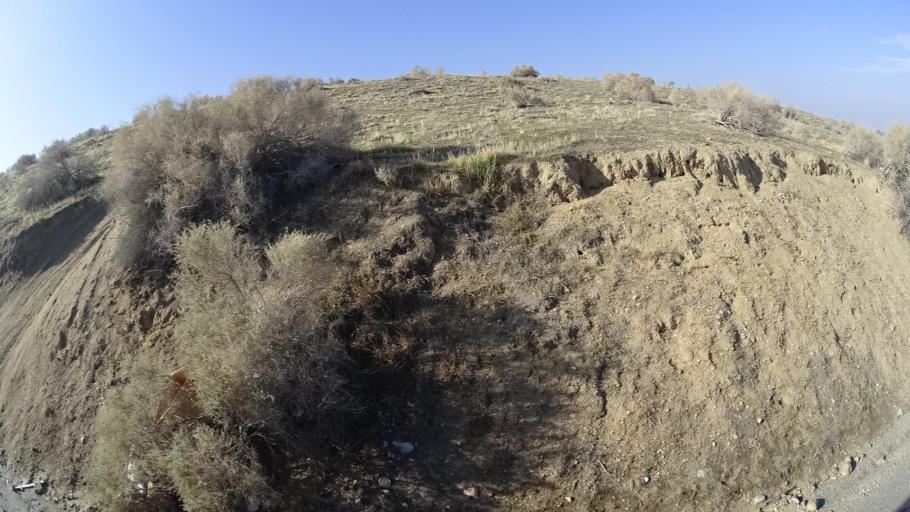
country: US
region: California
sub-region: Kern County
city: South Taft
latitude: 35.1275
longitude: -119.4564
